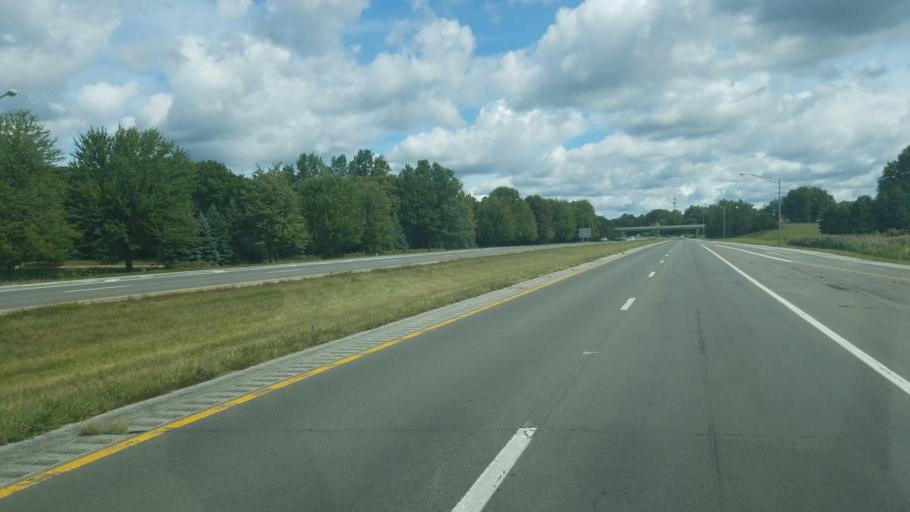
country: US
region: Ohio
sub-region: Lorain County
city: North Ridgeville
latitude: 41.3539
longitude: -82.0232
